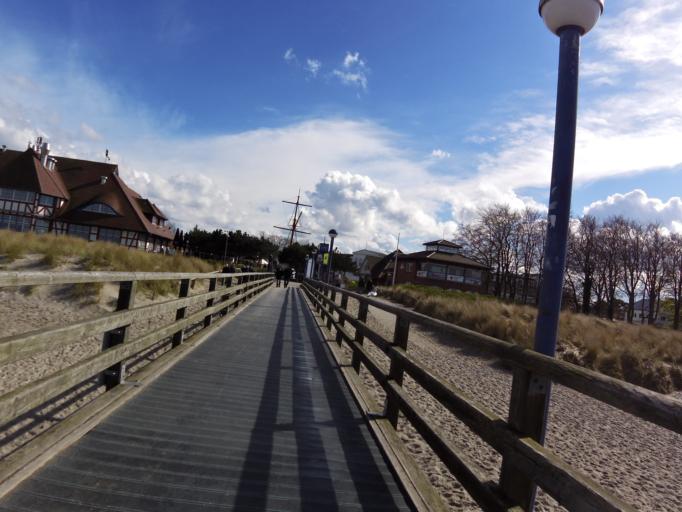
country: DE
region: Mecklenburg-Vorpommern
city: Zingst
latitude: 54.4416
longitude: 12.6816
